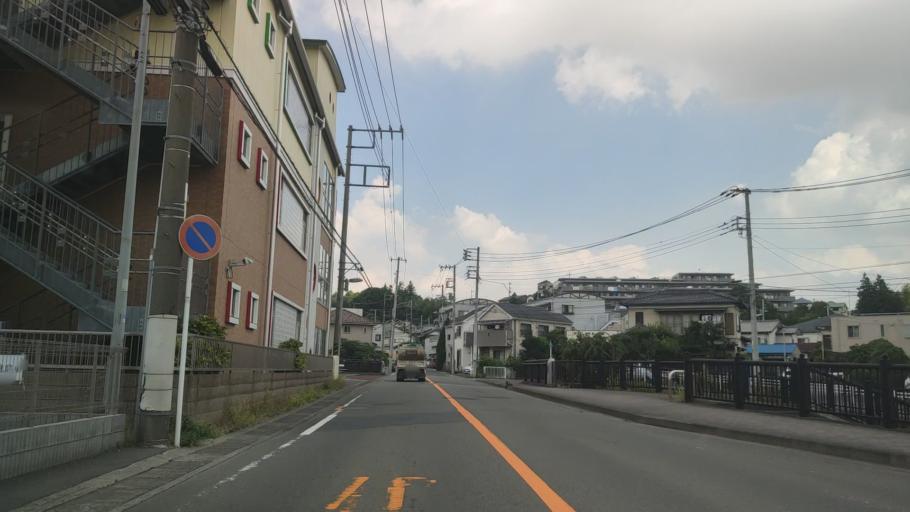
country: JP
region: Kanagawa
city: Minami-rinkan
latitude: 35.4356
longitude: 139.5135
